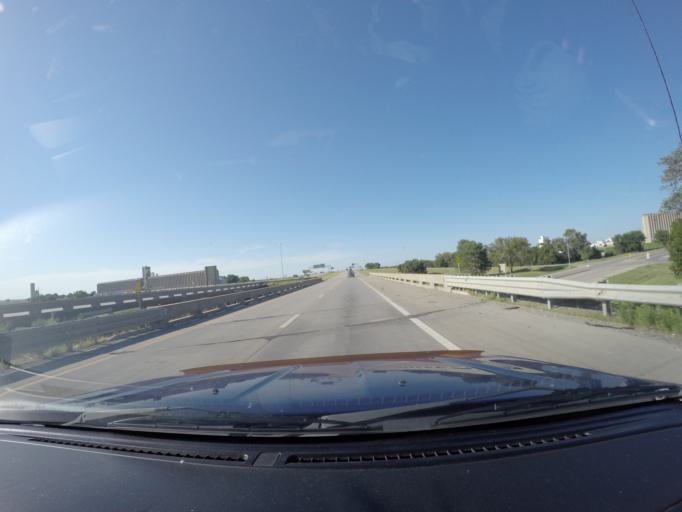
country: US
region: Kansas
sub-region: Shawnee County
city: Topeka
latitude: 39.0806
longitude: -95.7304
